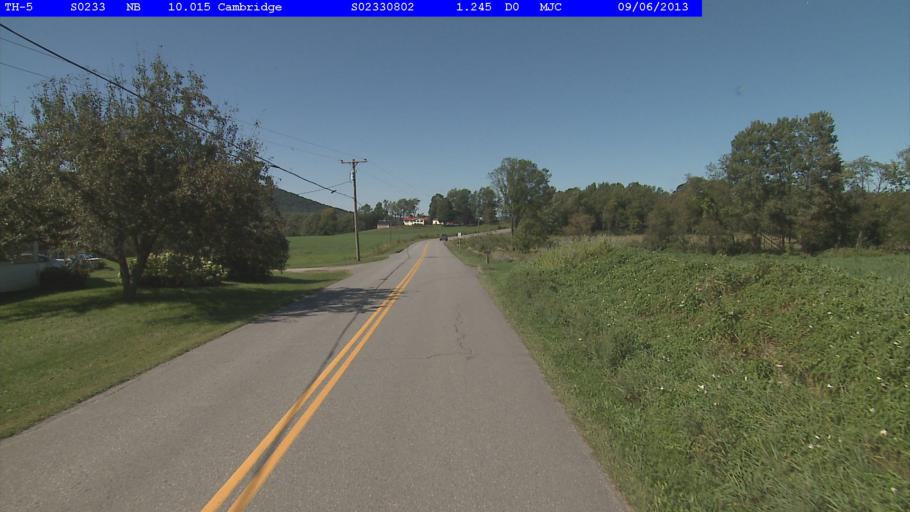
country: US
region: Vermont
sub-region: Chittenden County
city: Jericho
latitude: 44.6000
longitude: -72.8556
